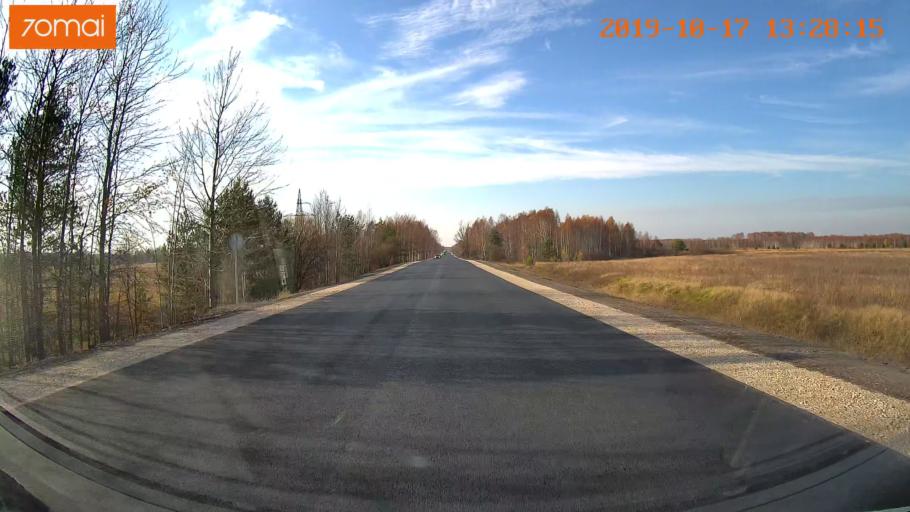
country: RU
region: Vladimir
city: Velikodvorskiy
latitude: 55.1156
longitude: 40.8737
